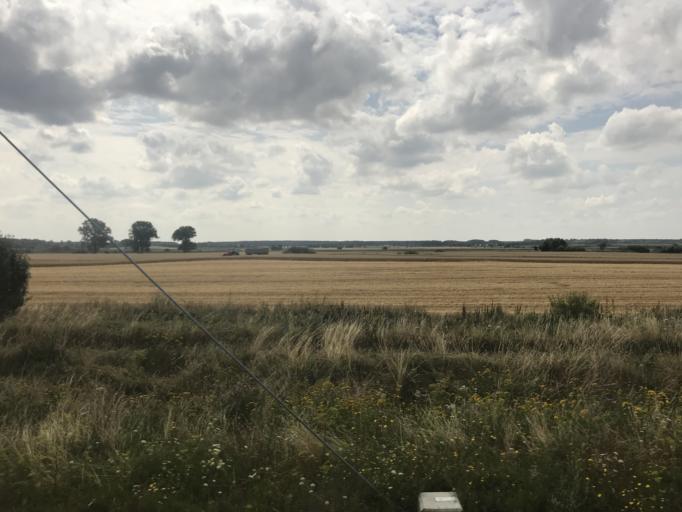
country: PL
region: Greater Poland Voivodeship
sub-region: Powiat poznanski
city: Pobiedziska
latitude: 52.4887
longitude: 17.3449
